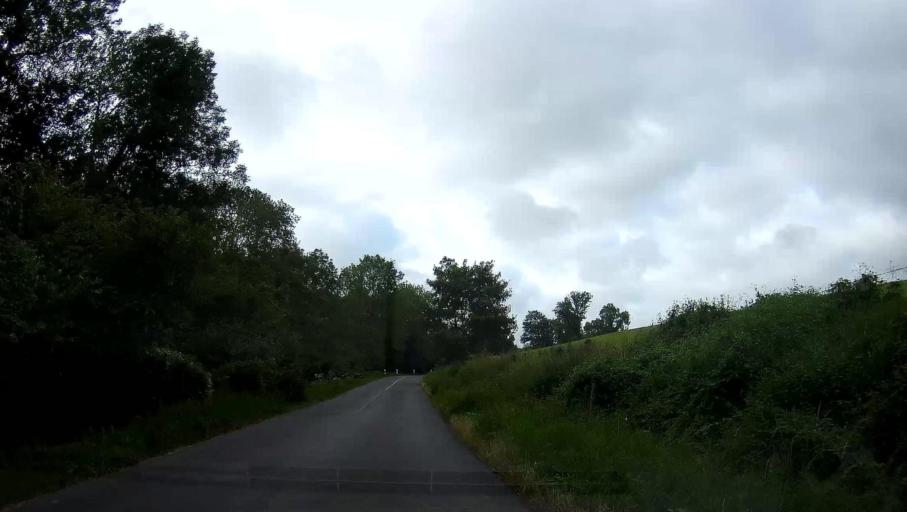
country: FR
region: Champagne-Ardenne
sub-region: Departement des Ardennes
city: Chateau-Porcien
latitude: 49.6309
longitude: 4.2402
